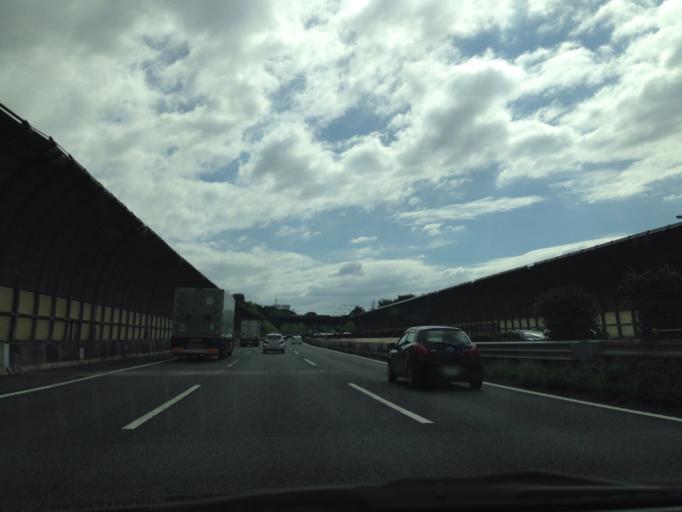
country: JP
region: Kanagawa
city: Hadano
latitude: 35.3681
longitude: 139.2608
